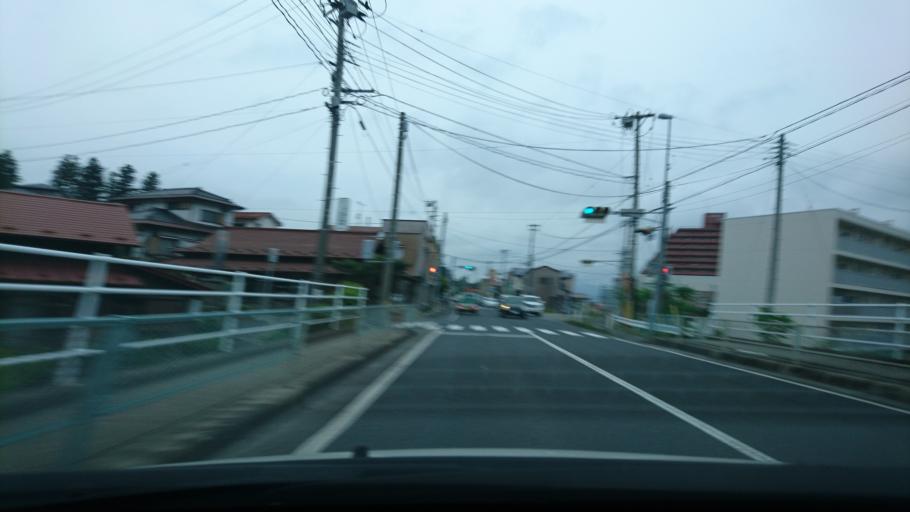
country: JP
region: Iwate
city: Ichinoseki
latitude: 38.9168
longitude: 141.1318
